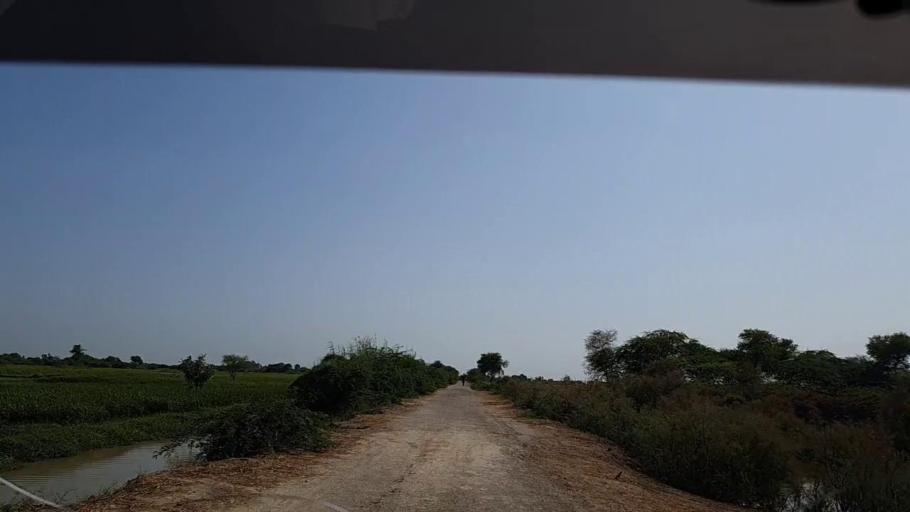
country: PK
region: Sindh
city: Badin
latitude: 24.6307
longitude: 68.7833
